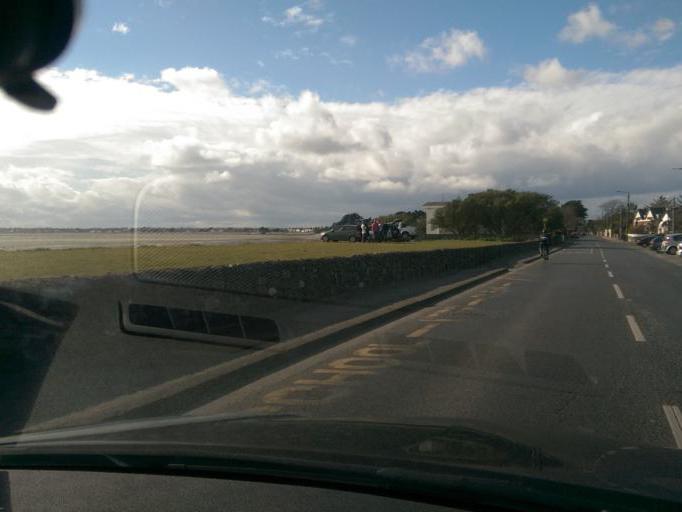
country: IE
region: Leinster
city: Sutton
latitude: 53.3866
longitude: -6.1034
